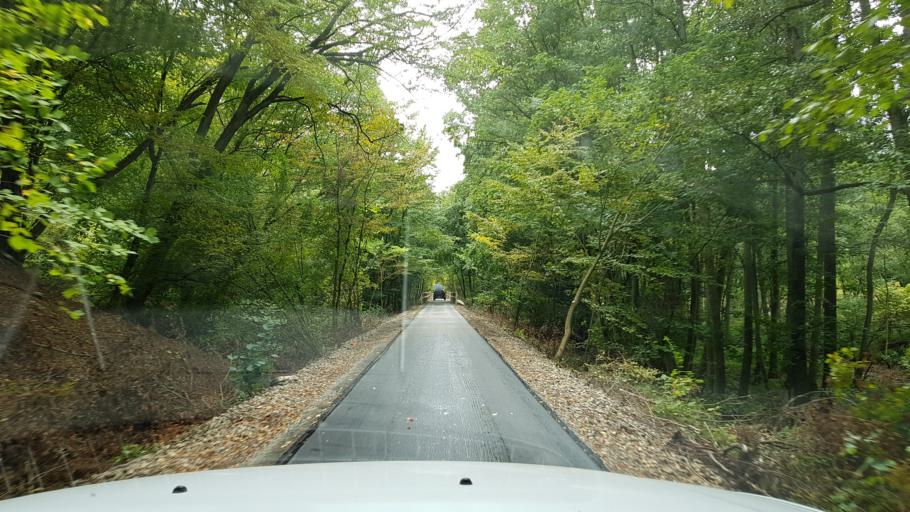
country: PL
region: West Pomeranian Voivodeship
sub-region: Powiat gryfinski
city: Cedynia
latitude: 52.8289
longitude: 14.2438
